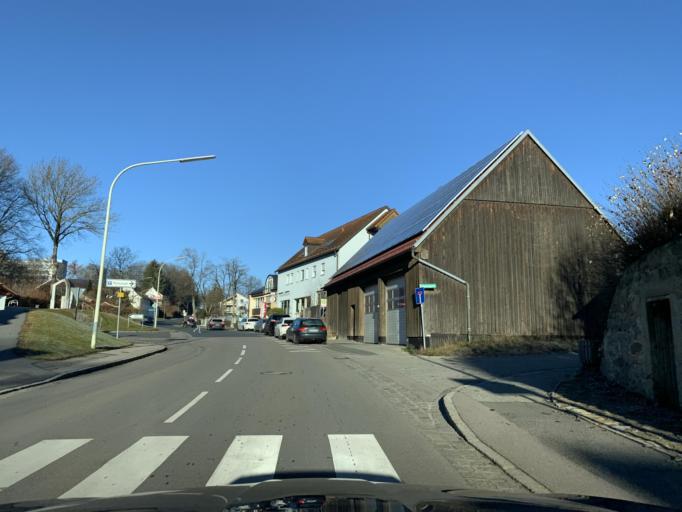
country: DE
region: Bavaria
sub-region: Upper Palatinate
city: Oberviechtach
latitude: 49.4600
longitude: 12.4165
